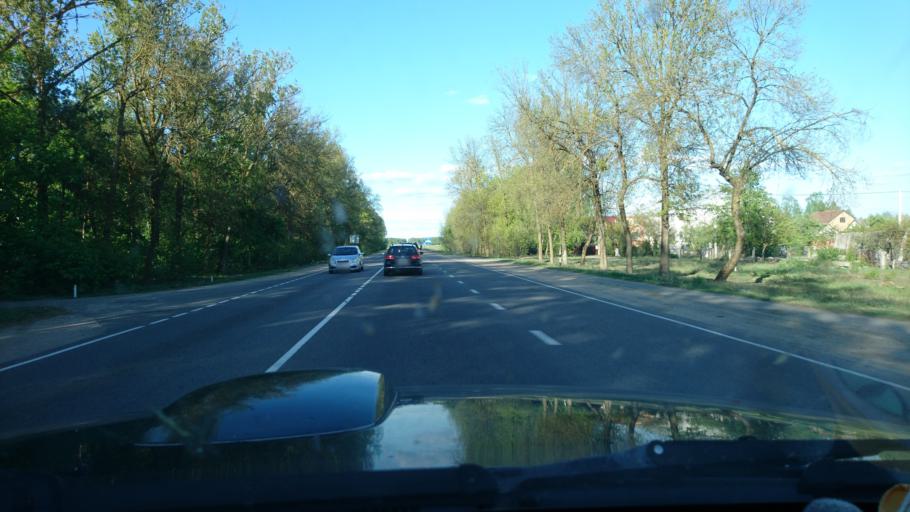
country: BY
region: Brest
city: Byaroza
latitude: 52.5478
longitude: 25.0118
